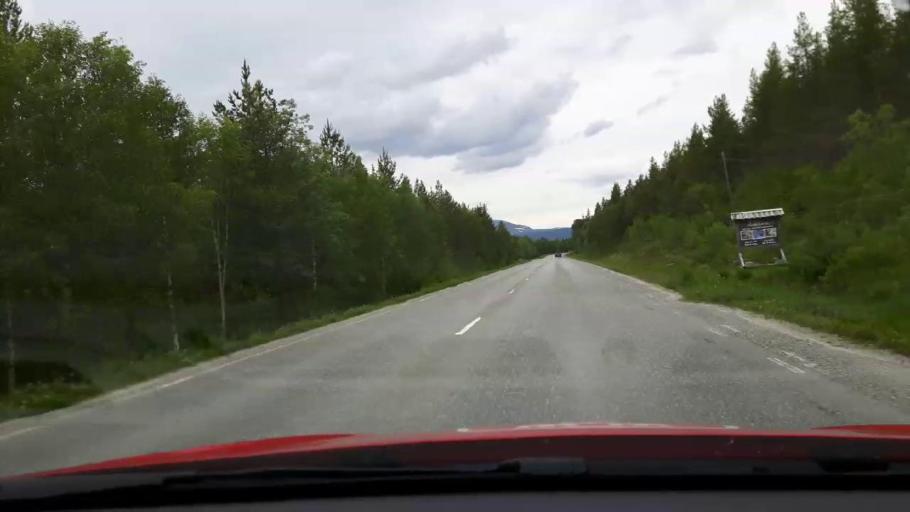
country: NO
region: Hedmark
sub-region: Engerdal
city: Engerdal
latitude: 62.5320
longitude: 12.5651
